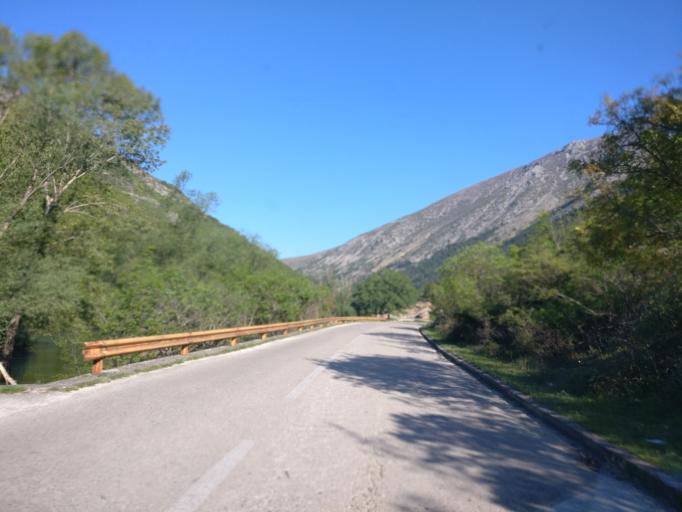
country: BA
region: Federation of Bosnia and Herzegovina
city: Stolac
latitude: 43.0897
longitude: 17.9990
